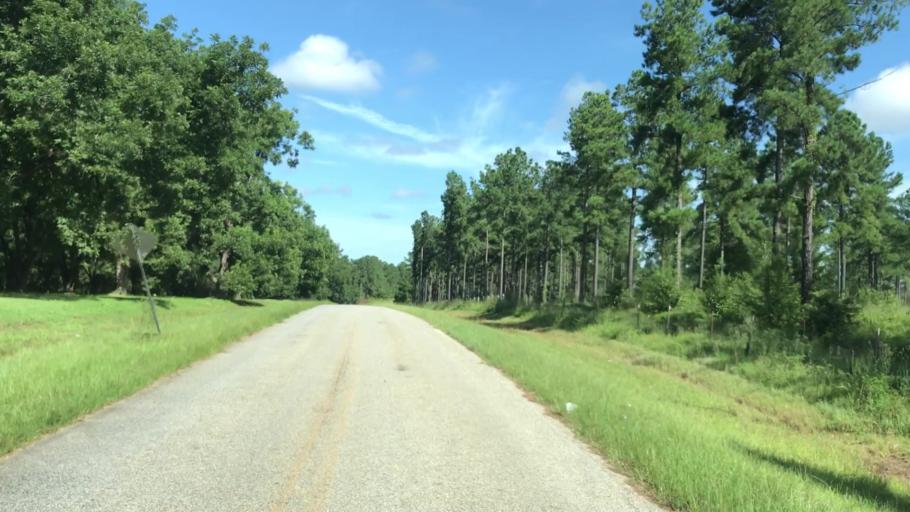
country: US
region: Georgia
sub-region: Jefferson County
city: Wadley
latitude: 32.8007
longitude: -82.3656
